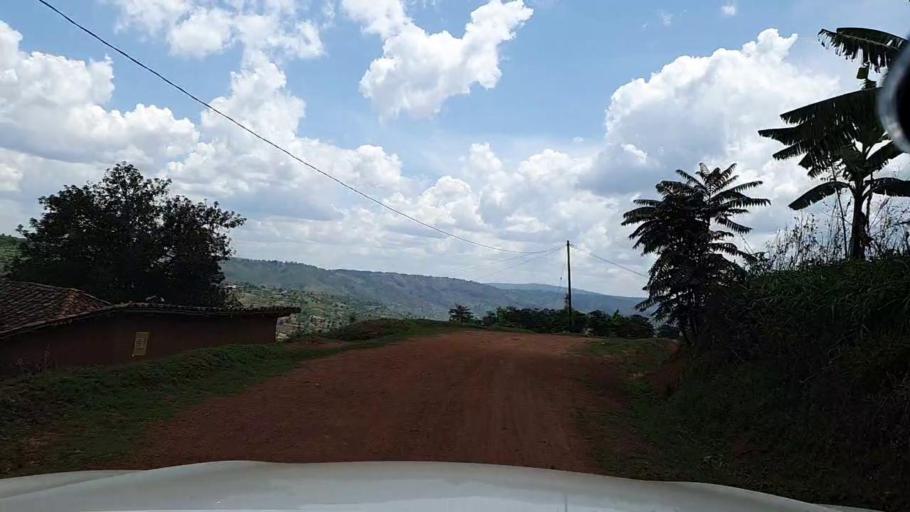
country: RW
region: Southern Province
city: Butare
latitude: -2.7580
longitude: 29.7474
